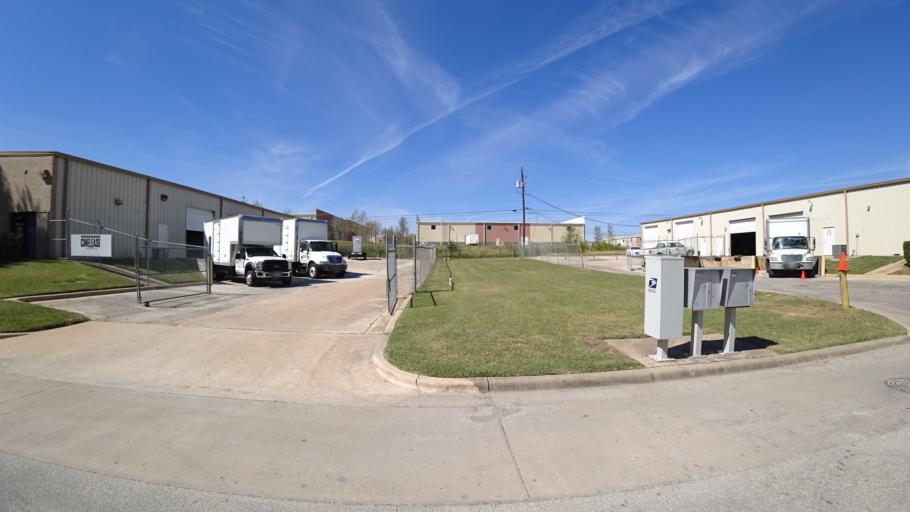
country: US
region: Texas
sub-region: Travis County
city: Austin
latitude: 30.1934
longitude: -97.7027
